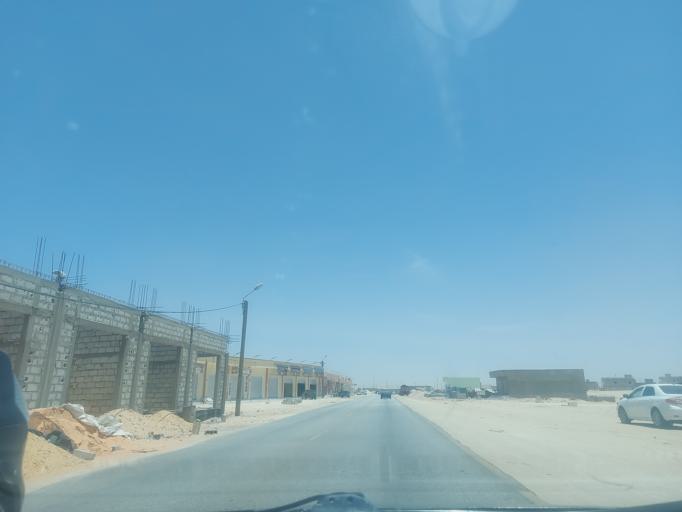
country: MR
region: Nouakchott
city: Nouakchott
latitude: 18.0840
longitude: -15.9526
